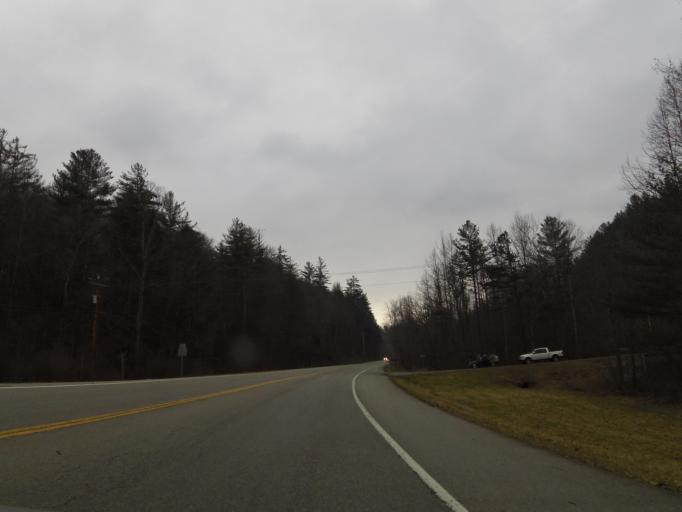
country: US
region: Tennessee
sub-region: Roane County
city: Harriman
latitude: 36.0184
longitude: -84.5267
